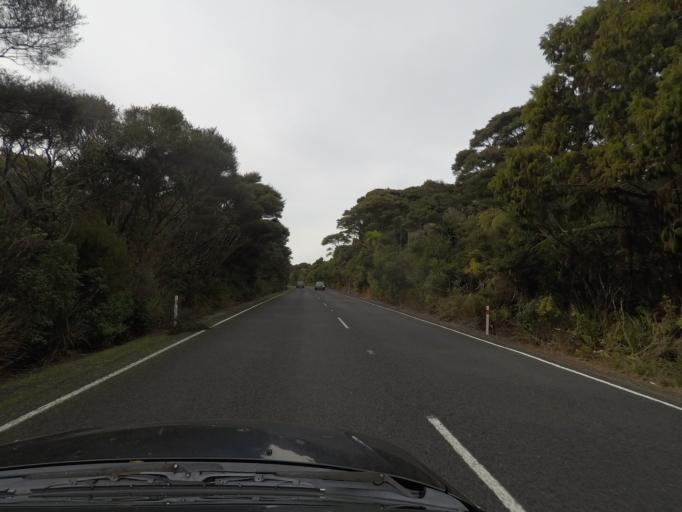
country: NZ
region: Auckland
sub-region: Auckland
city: Titirangi
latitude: -36.9440
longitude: 174.5474
